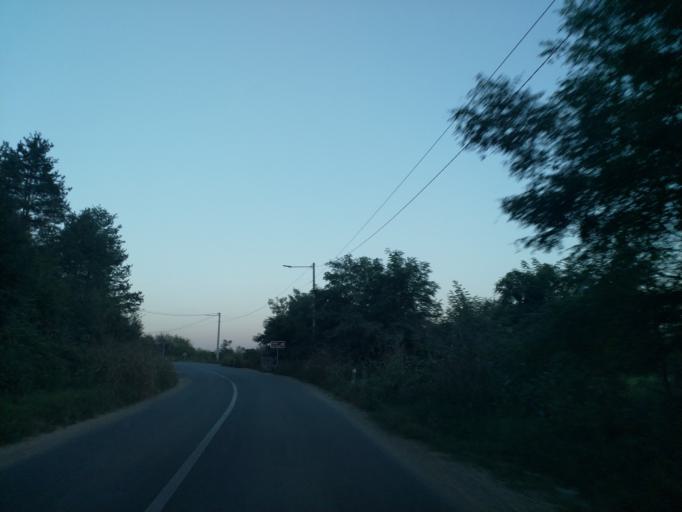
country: RS
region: Central Serbia
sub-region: Rasinski Okrug
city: Krusevac
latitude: 43.6266
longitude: 21.3369
